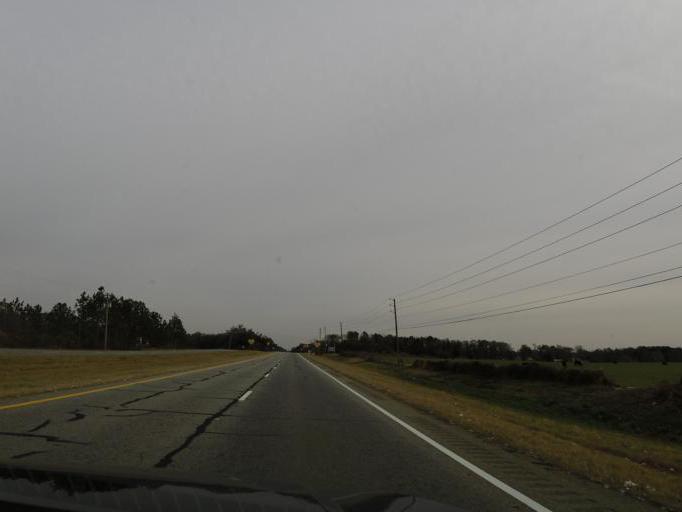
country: US
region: Georgia
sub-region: Decatur County
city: Bainbridge
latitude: 30.9349
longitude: -84.6528
